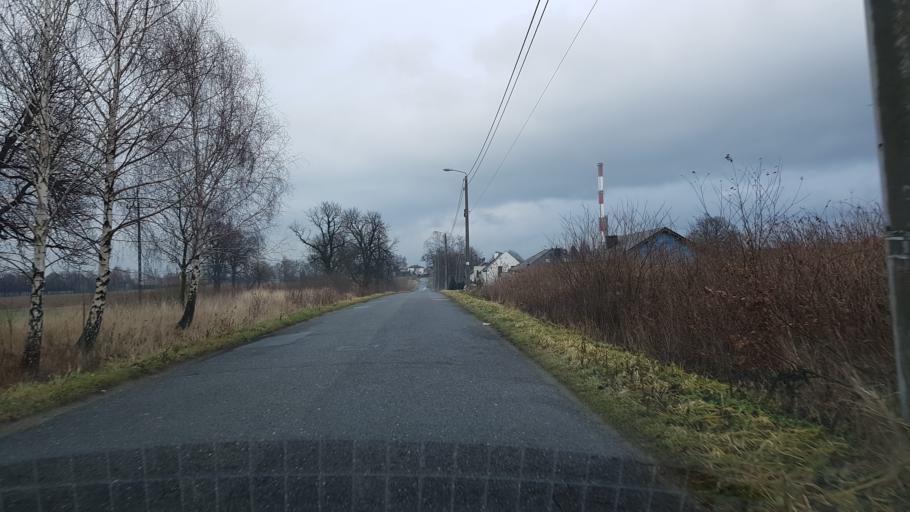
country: PL
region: Silesian Voivodeship
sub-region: Powiat pszczynski
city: Pszczyna
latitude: 49.9664
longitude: 18.9135
